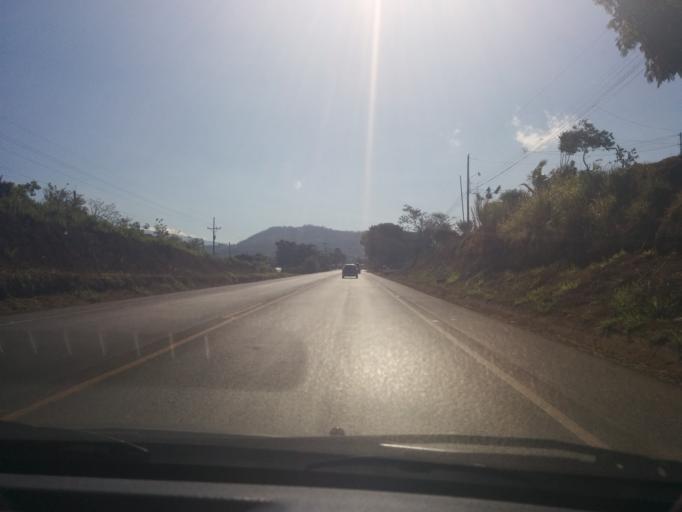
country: CR
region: Alajuela
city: San Rafael
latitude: 10.0762
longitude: -84.4743
